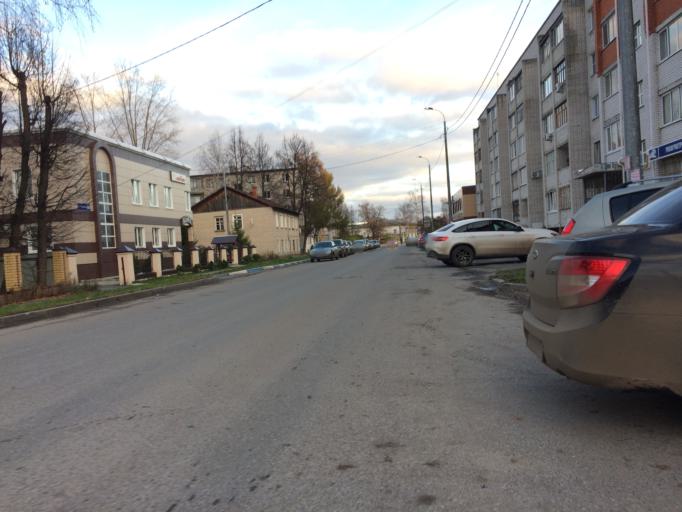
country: RU
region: Mariy-El
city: Yoshkar-Ola
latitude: 56.6470
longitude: 47.8981
